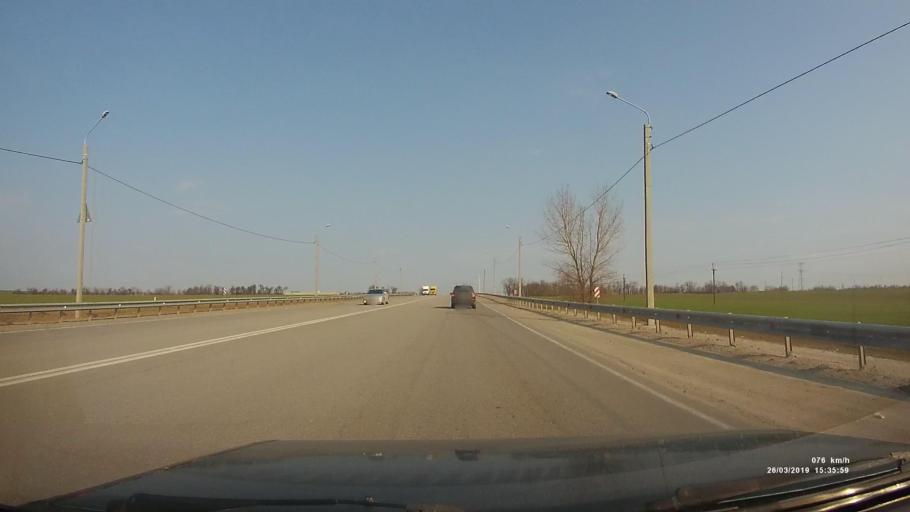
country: RU
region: Rostov
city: Sinyavskoye
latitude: 47.2987
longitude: 39.2216
